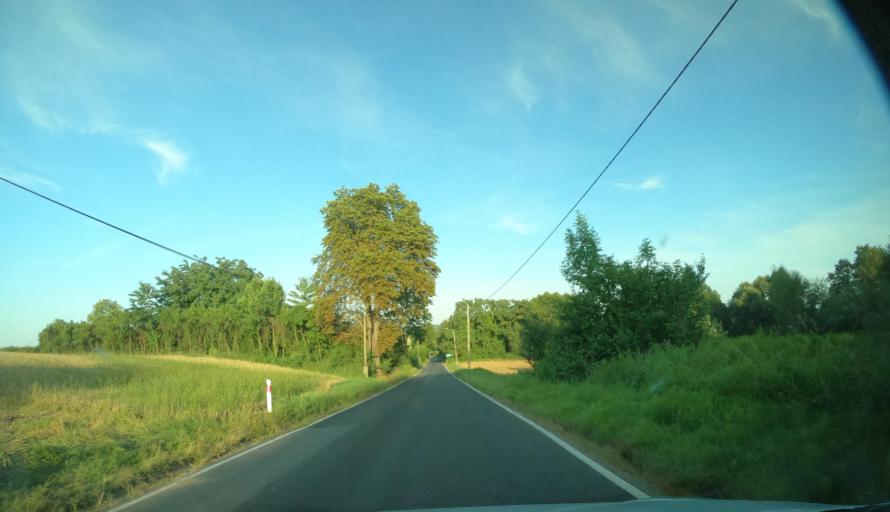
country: PL
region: Kujawsko-Pomorskie
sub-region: Bydgoszcz
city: Fordon
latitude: 53.2083
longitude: 18.1730
